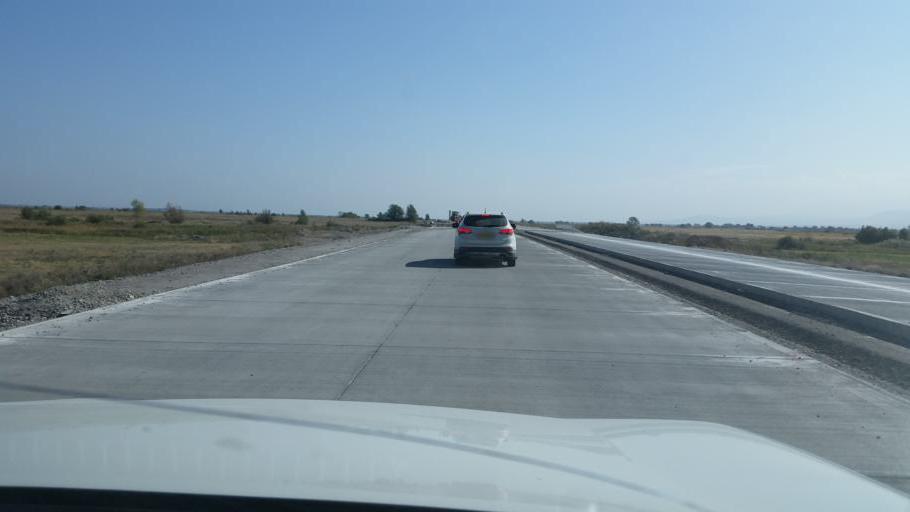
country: KZ
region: Almaty Oblysy
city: Turgen'
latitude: 43.5312
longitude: 77.6061
